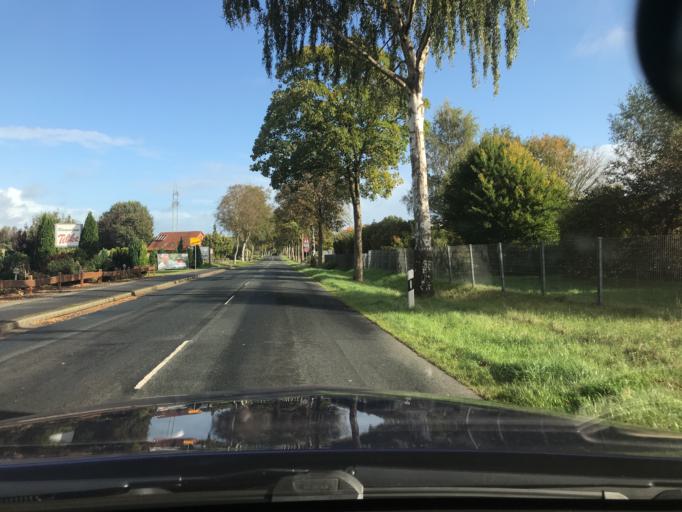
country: DE
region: Lower Saxony
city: Ahlerstedt
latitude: 53.4121
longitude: 9.4576
